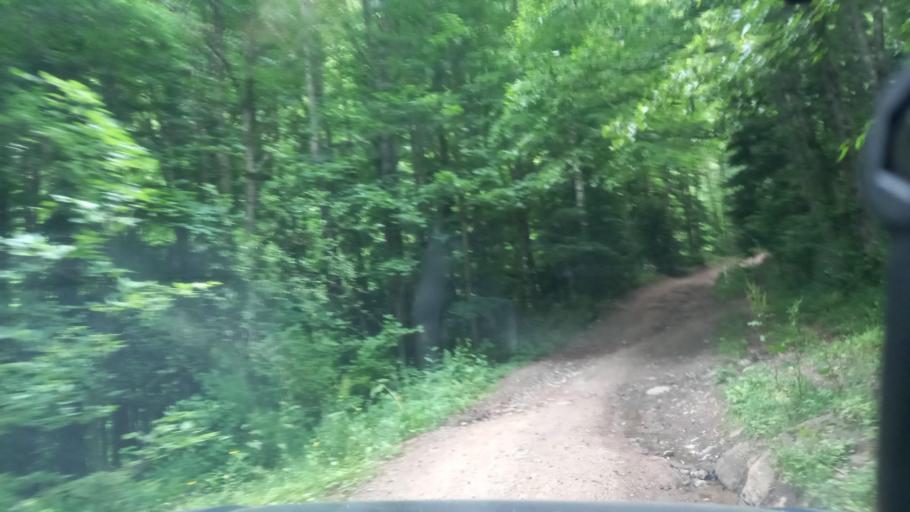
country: RU
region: Karachayevo-Cherkesiya
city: Kurdzhinovo
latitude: 43.8147
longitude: 40.8800
